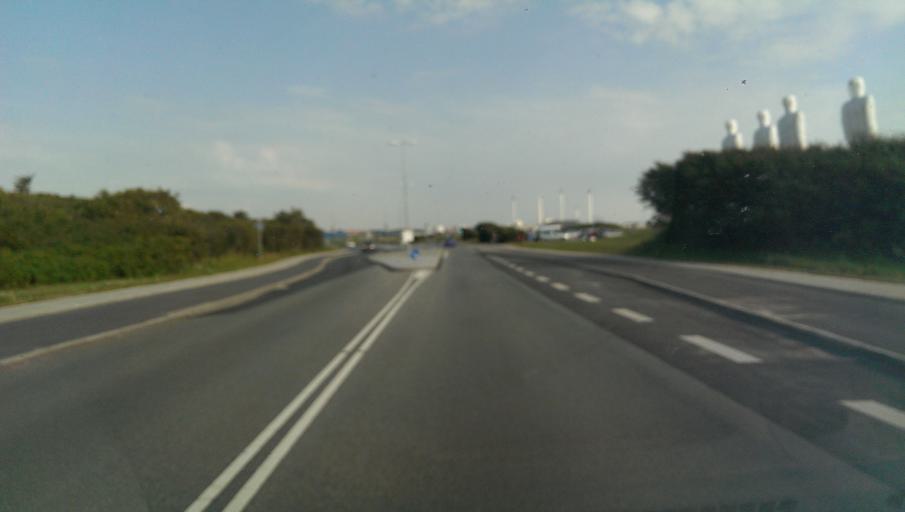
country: DK
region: South Denmark
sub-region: Fano Kommune
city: Nordby
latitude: 55.4885
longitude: 8.4105
